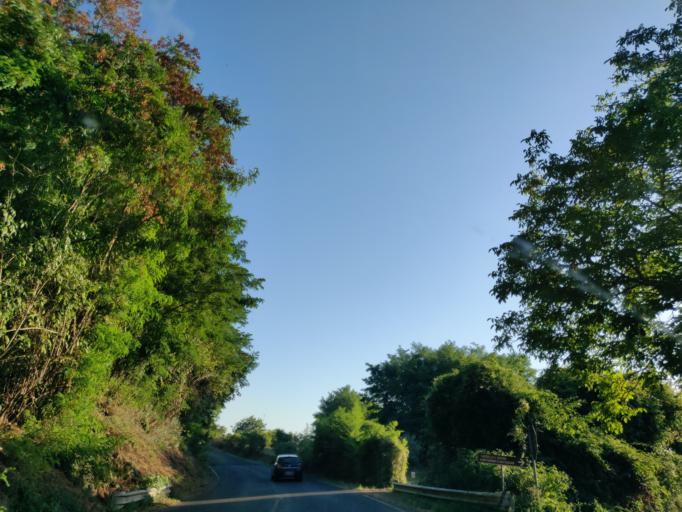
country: IT
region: Latium
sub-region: Provincia di Viterbo
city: Grotte di Castro
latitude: 42.6696
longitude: 11.8585
